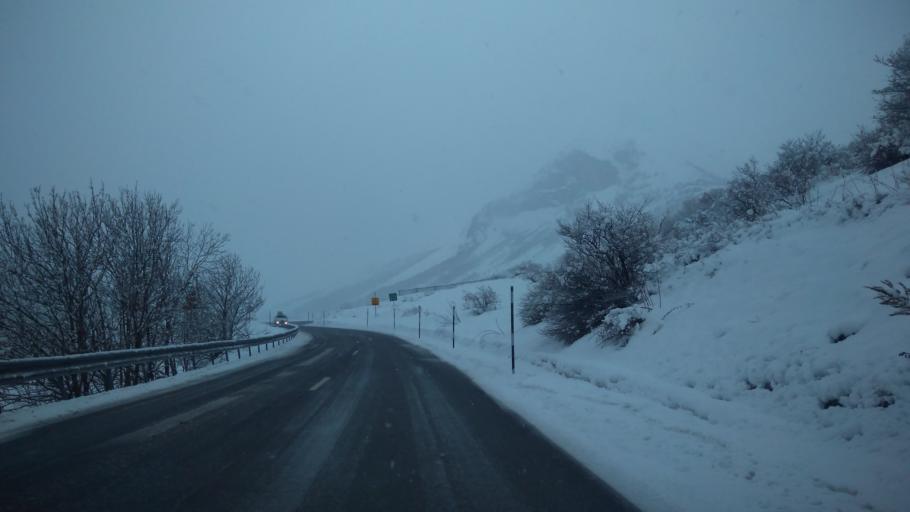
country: FR
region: Provence-Alpes-Cote d'Azur
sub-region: Departement des Hautes-Alpes
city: Le Monetier-les-Bains
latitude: 45.0120
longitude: 6.4691
